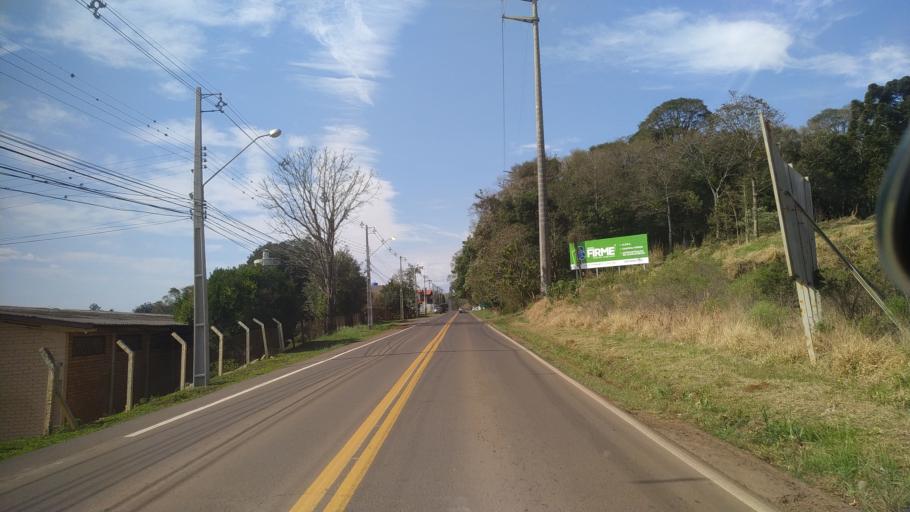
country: BR
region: Santa Catarina
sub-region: Chapeco
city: Chapeco
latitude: -27.1090
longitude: -52.5934
